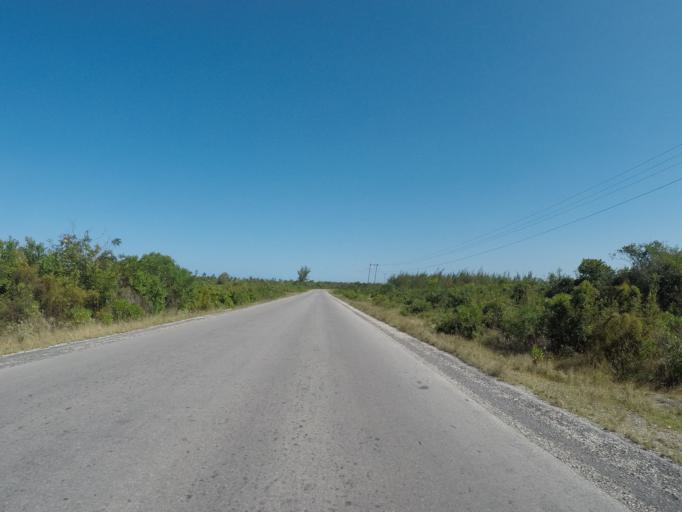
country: TZ
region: Zanzibar Central/South
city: Nganane
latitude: -6.2057
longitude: 39.5306
